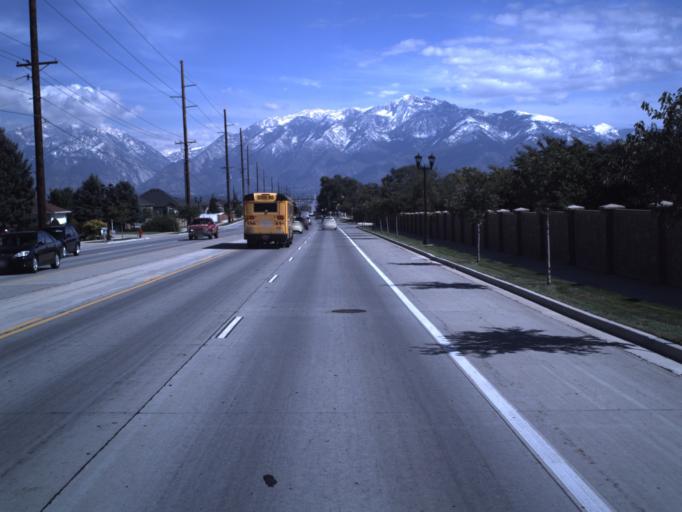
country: US
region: Utah
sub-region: Salt Lake County
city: South Jordan Heights
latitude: 40.5440
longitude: -111.9699
